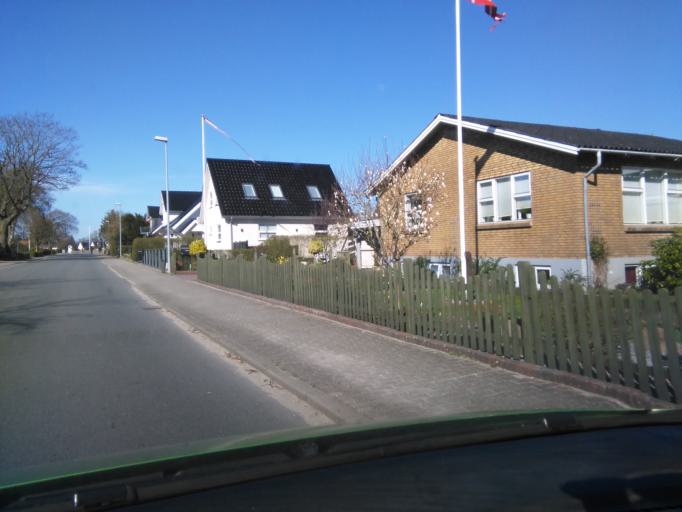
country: DK
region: South Denmark
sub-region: Varde Kommune
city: Oksbol
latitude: 55.6291
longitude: 8.2792
